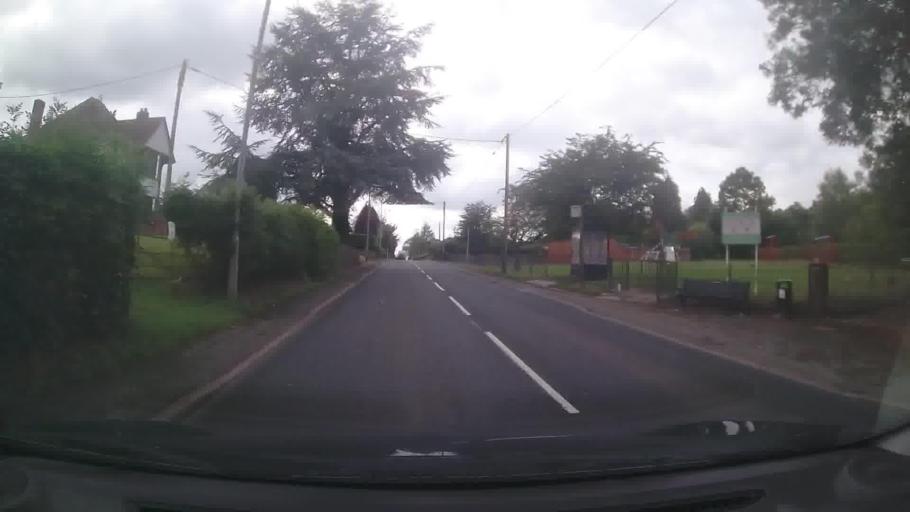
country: GB
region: England
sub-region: Shropshire
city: Pant
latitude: 52.7911
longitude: -3.0773
